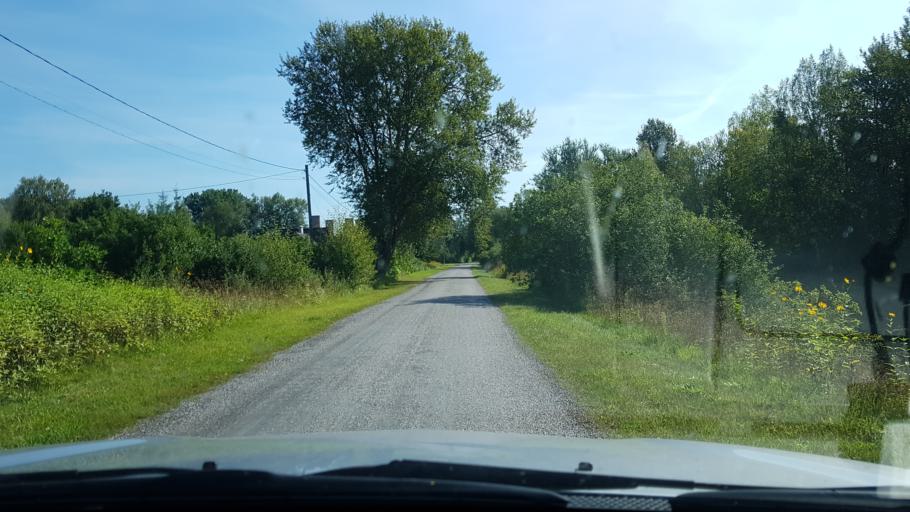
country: EE
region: Ida-Virumaa
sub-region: Sillamaee linn
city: Sillamae
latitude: 59.3376
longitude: 27.6825
